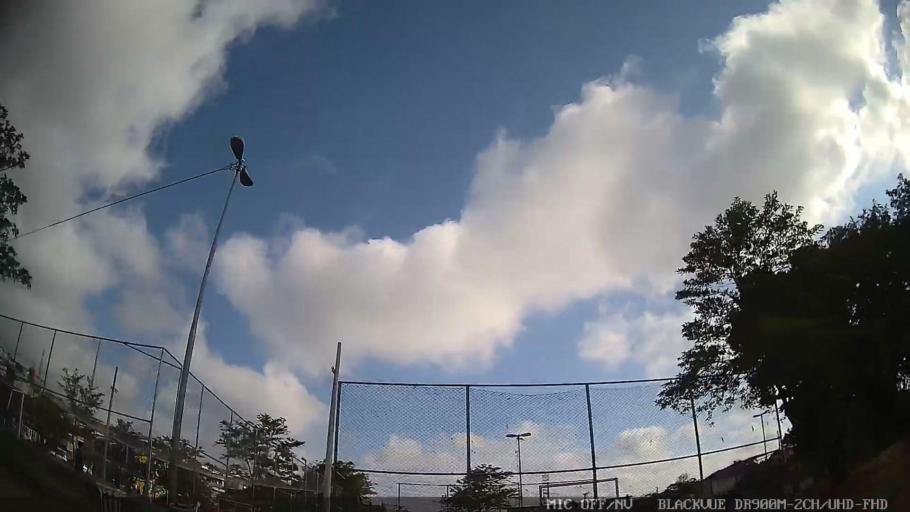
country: BR
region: Sao Paulo
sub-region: Sao Caetano Do Sul
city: Sao Caetano do Sul
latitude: -23.5765
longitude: -46.5213
